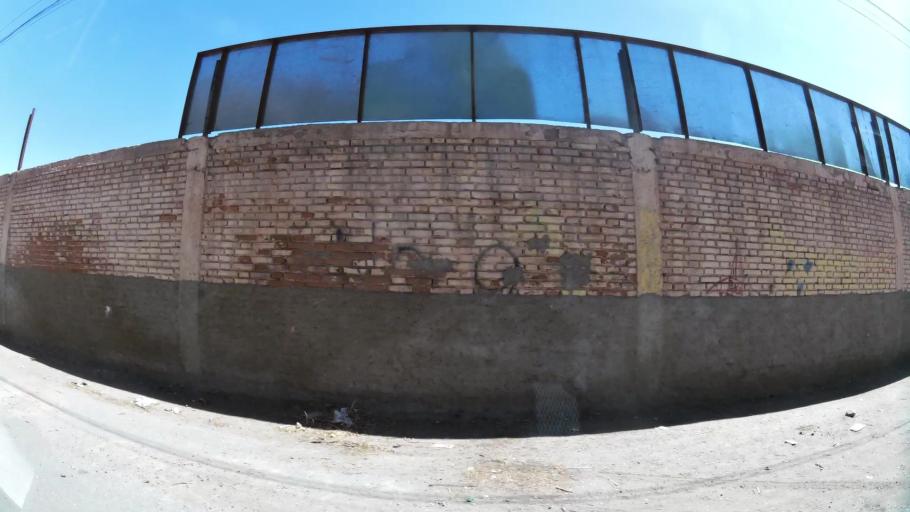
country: AR
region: Mendoza
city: Villa Nueva
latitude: -32.8695
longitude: -68.7855
